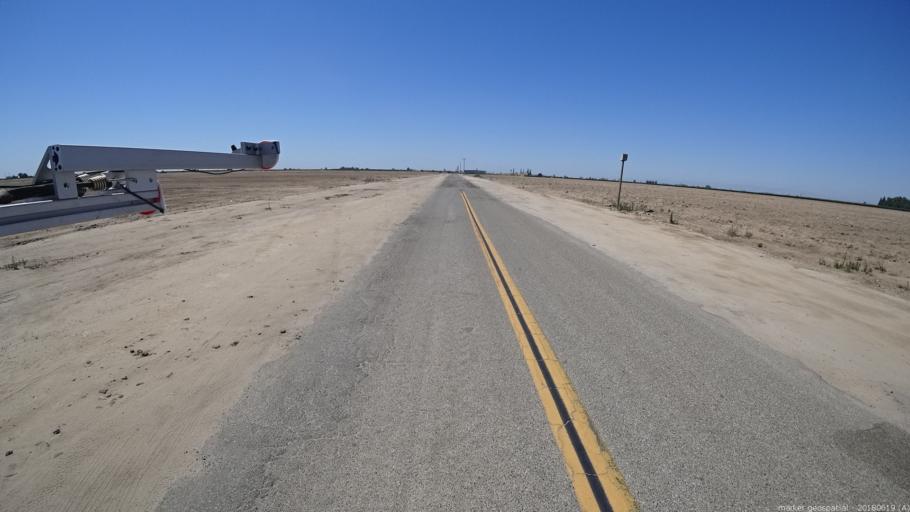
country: US
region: California
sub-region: Fresno County
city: Biola
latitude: 36.8509
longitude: -120.0650
